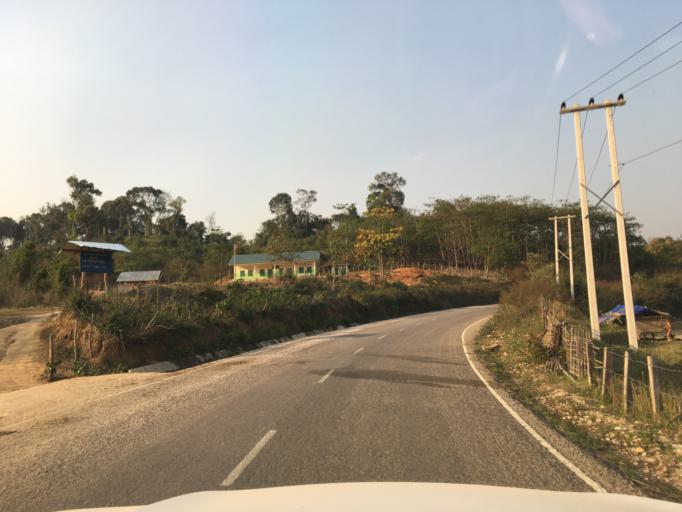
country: LA
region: Houaphan
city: Xam Nua
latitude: 20.6016
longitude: 104.0690
